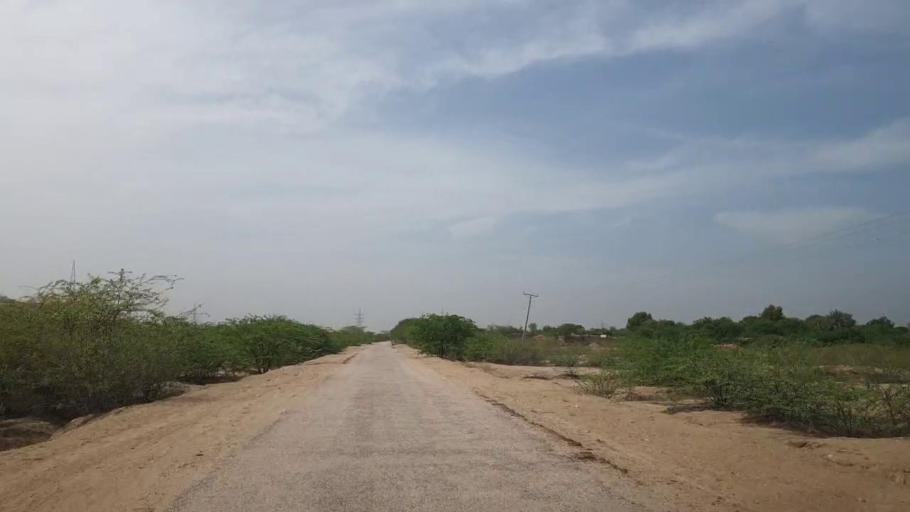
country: PK
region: Sindh
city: Kot Diji
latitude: 27.3675
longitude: 68.7645
